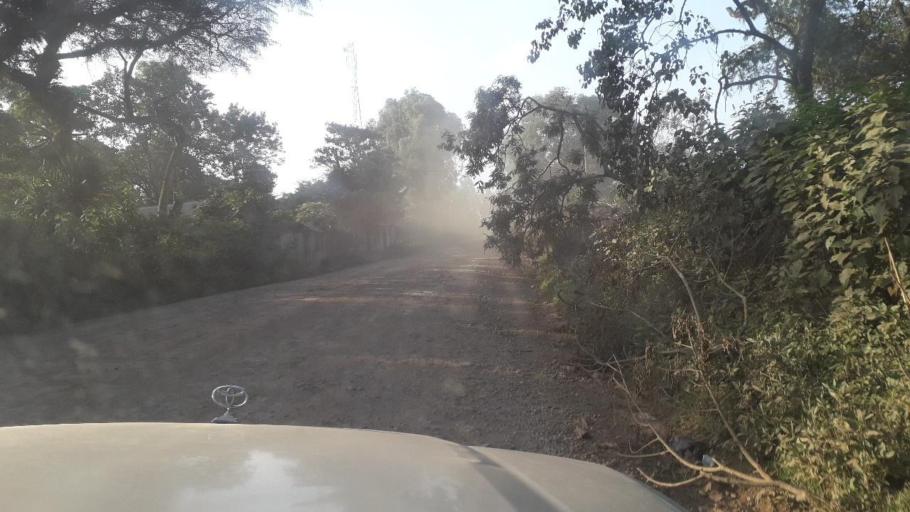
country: ET
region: Oromiya
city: Jima
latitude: 7.5994
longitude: 36.8453
